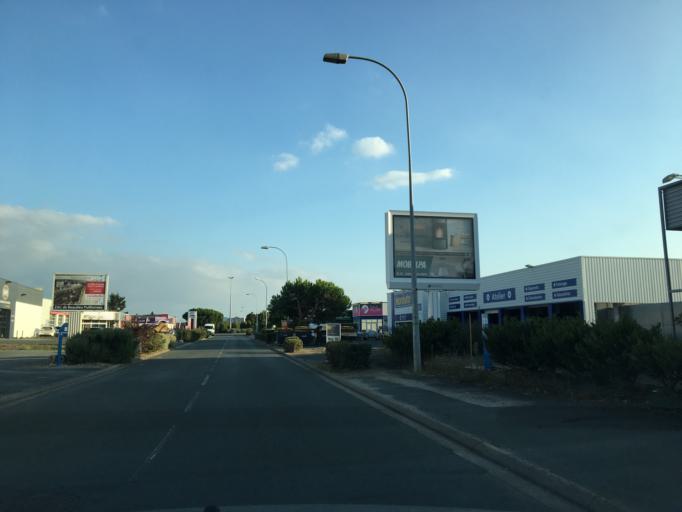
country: FR
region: Poitou-Charentes
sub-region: Departement de la Charente-Maritime
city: Angoulins
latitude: 46.1075
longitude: -1.1010
